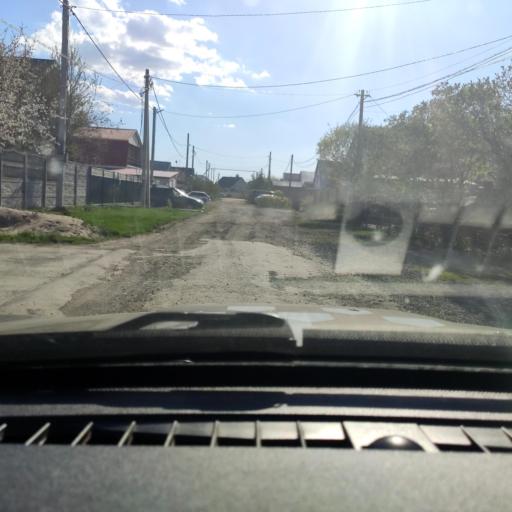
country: RU
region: Samara
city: Tol'yatti
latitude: 53.5655
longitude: 49.3792
